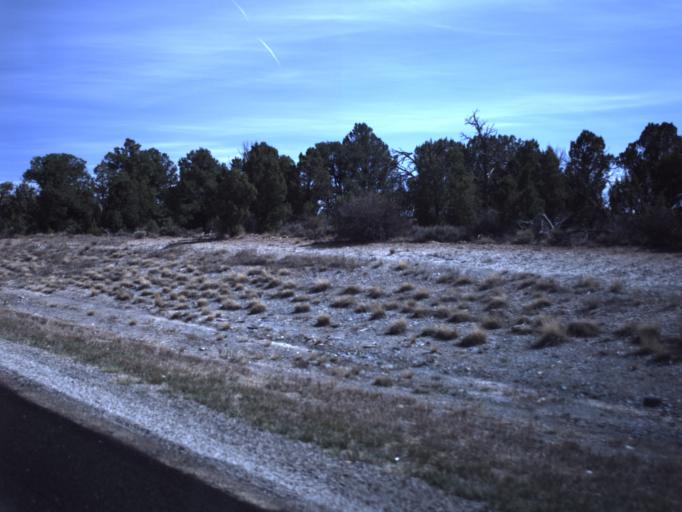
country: US
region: Colorado
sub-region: Dolores County
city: Dove Creek
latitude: 37.8243
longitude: -109.0694
